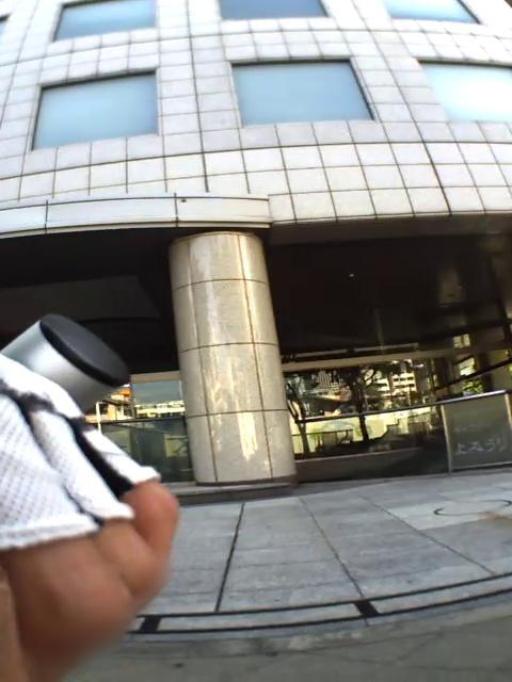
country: JP
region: Osaka
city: Osaka-shi
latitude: 34.7001
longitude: 135.5060
